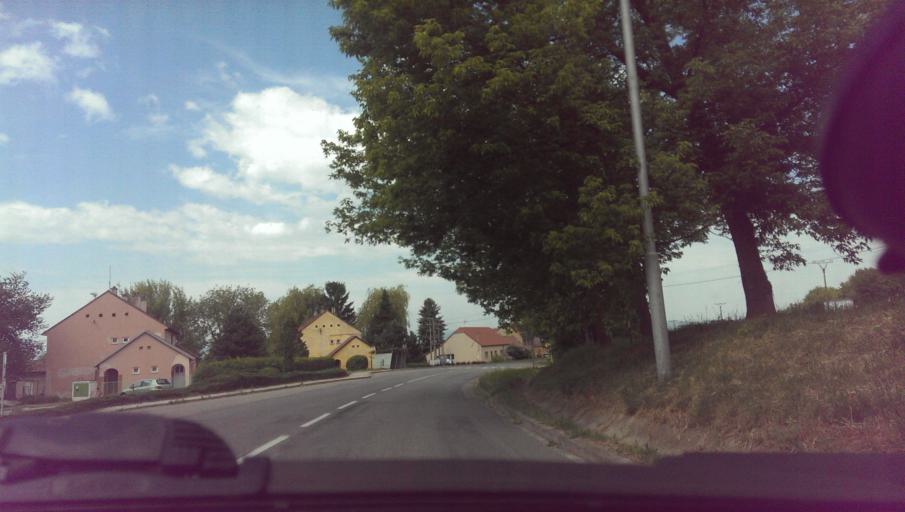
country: CZ
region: Zlin
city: Kunovice
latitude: 49.0293
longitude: 17.4693
